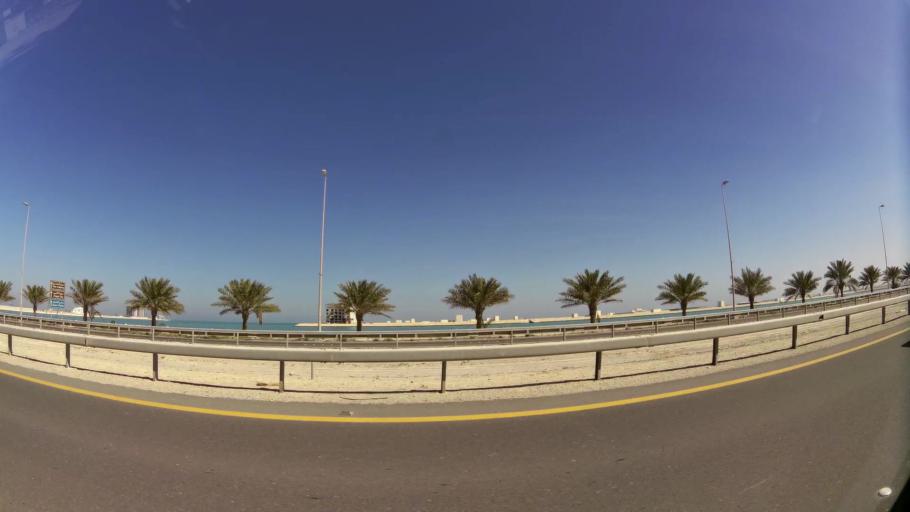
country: BH
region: Muharraq
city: Al Hadd
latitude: 26.2618
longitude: 50.6607
